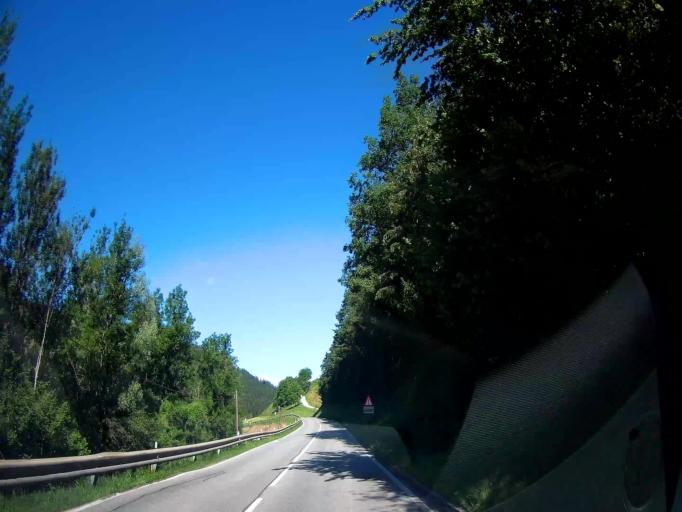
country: AT
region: Carinthia
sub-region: Politischer Bezirk Sankt Veit an der Glan
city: Bruckl
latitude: 46.7534
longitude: 14.5056
